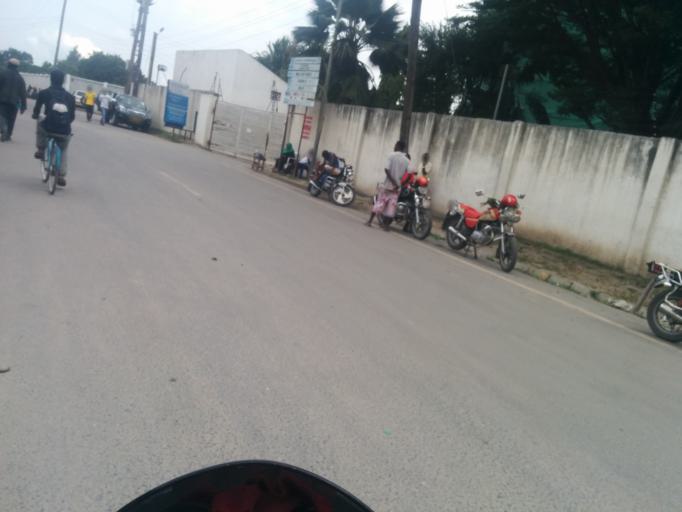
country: TZ
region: Dar es Salaam
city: Dar es Salaam
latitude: -6.8335
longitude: 39.2756
